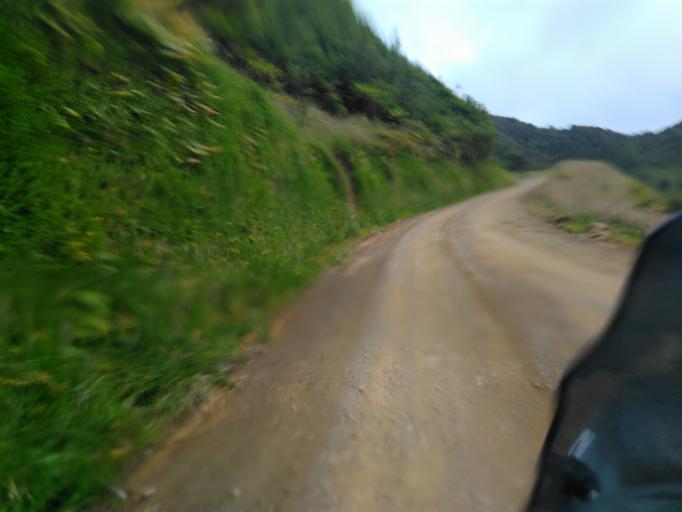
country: NZ
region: Bay of Plenty
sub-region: Opotiki District
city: Opotiki
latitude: -38.0960
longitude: 177.4856
